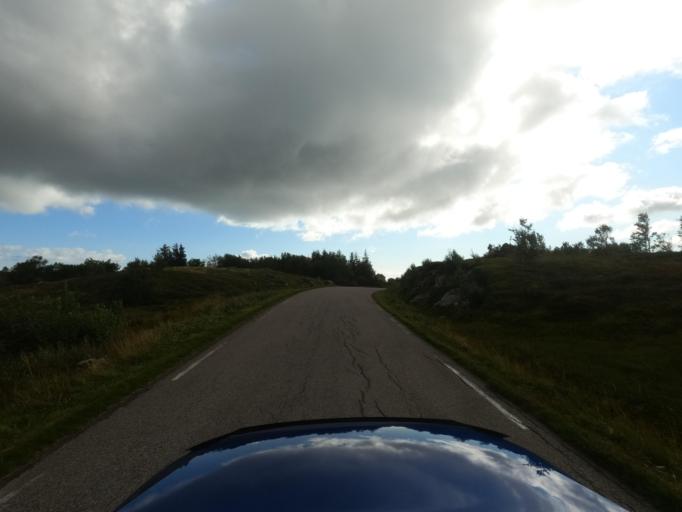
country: NO
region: Nordland
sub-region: Vestvagoy
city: Evjen
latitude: 68.1850
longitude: 13.8596
